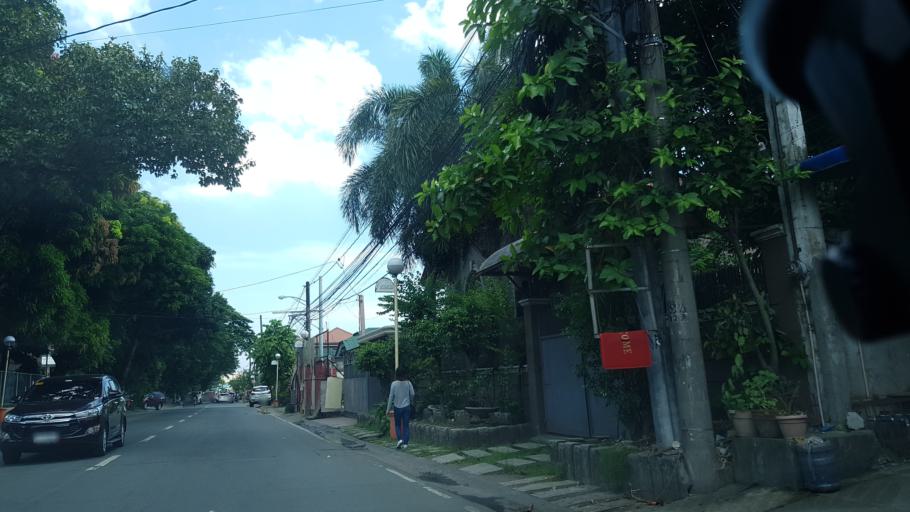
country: PH
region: Calabarzon
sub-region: Province of Rizal
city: Las Pinas
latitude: 14.4327
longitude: 120.9856
